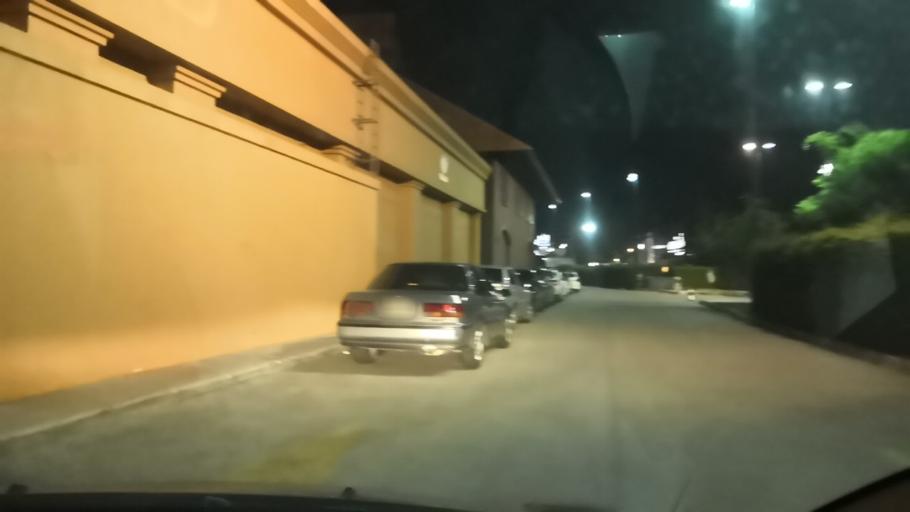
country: TH
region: Chiang Mai
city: Hang Dong
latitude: 18.6996
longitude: 98.9315
